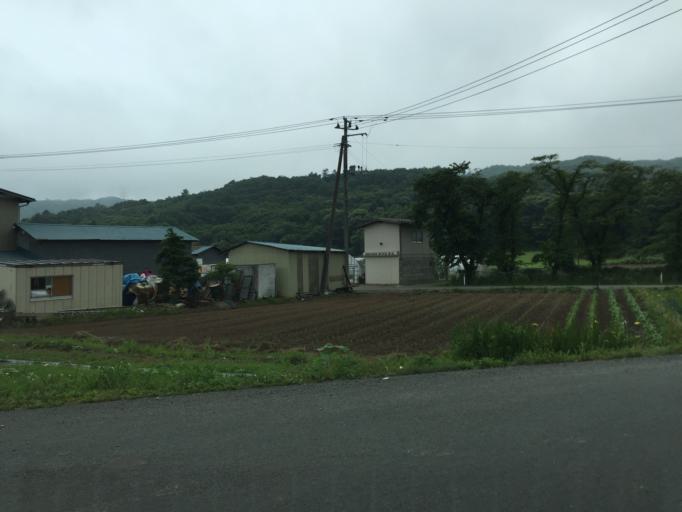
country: JP
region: Miyagi
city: Marumori
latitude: 37.7648
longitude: 140.7362
